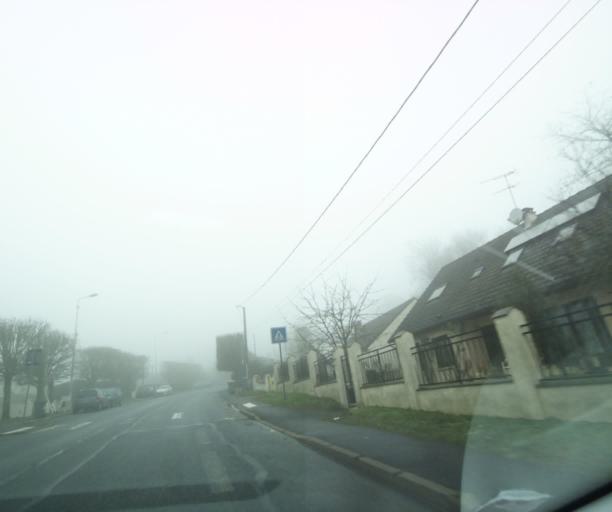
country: FR
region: Ile-de-France
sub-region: Departement de Seine-et-Marne
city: Dammartin-en-Goele
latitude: 49.0535
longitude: 2.6925
